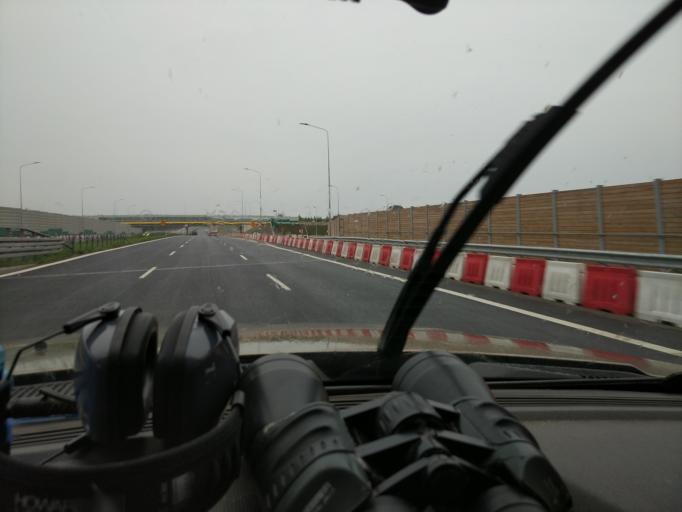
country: PL
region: Masovian Voivodeship
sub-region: Powiat wolominski
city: Kobylka
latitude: 52.3690
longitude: 21.1891
